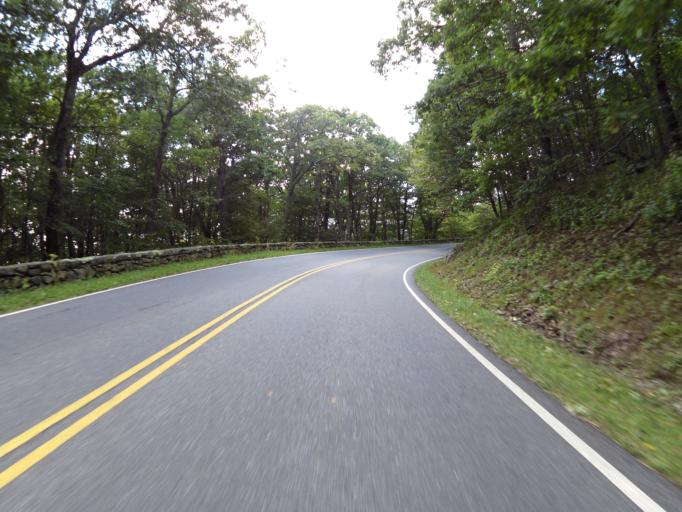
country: US
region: Virginia
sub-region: Page County
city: Stanley
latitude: 38.5567
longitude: -78.3794
